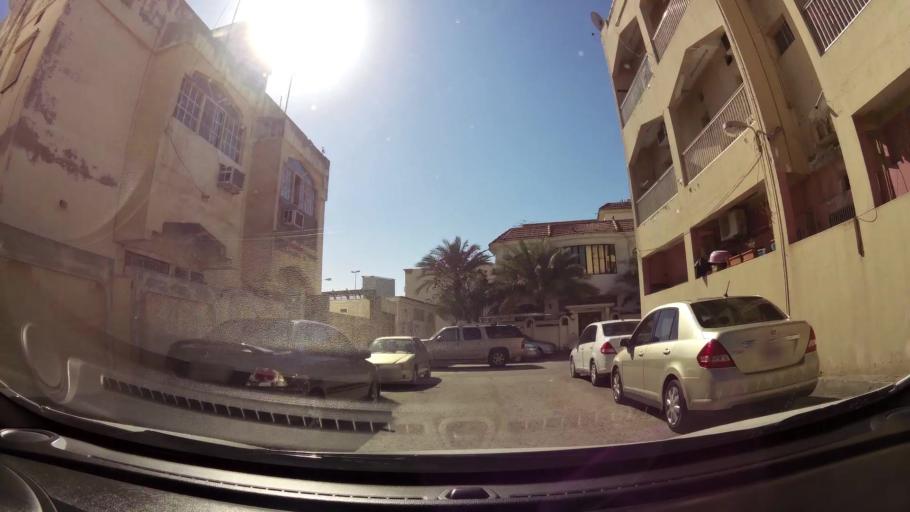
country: BH
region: Muharraq
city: Al Muharraq
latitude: 26.2637
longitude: 50.6205
